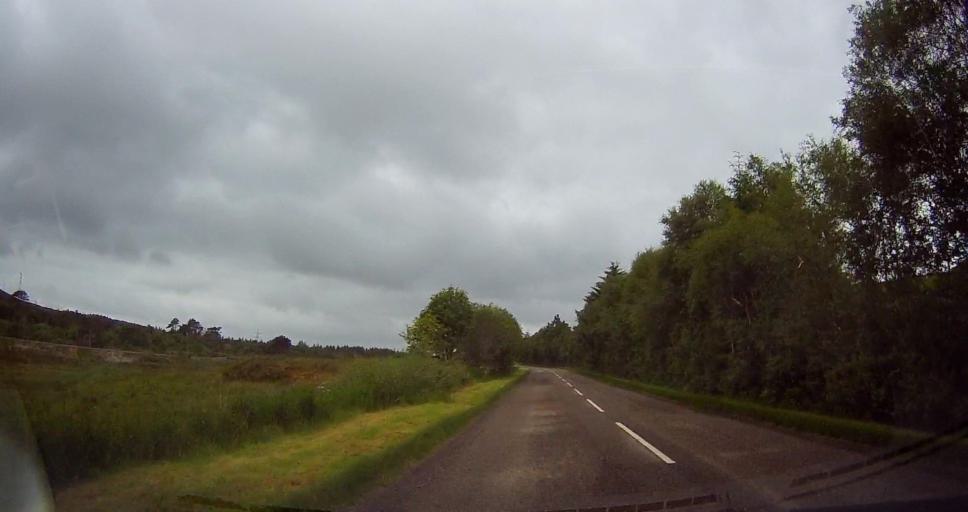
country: GB
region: Scotland
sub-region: Highland
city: Alness
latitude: 58.0188
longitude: -4.3393
